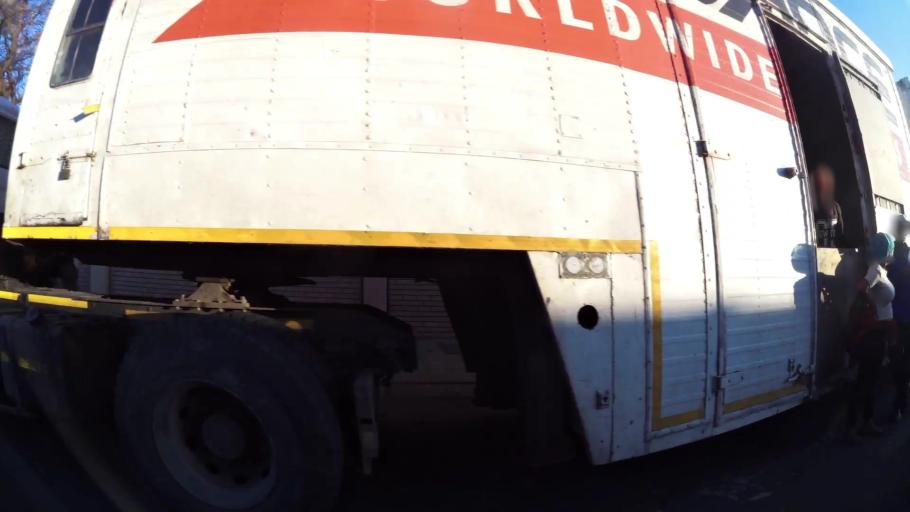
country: ZA
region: Northern Cape
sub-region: Frances Baard District Municipality
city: Kimberley
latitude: -28.7422
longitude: 24.7661
